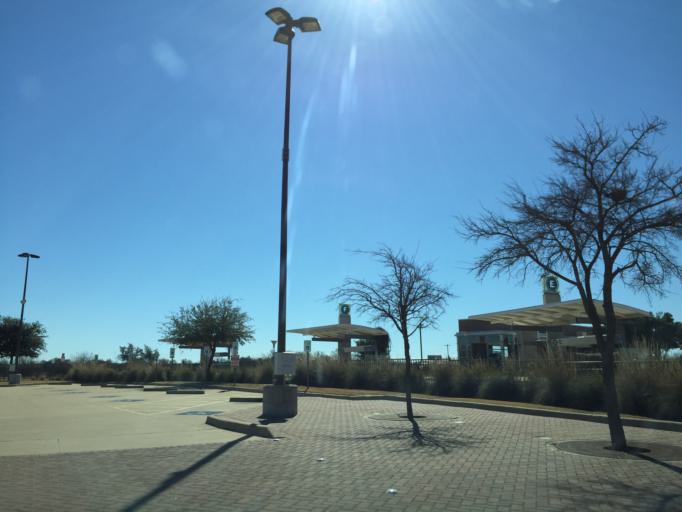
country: US
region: Texas
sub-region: Williamson County
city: Leander
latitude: 30.5866
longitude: -97.8552
